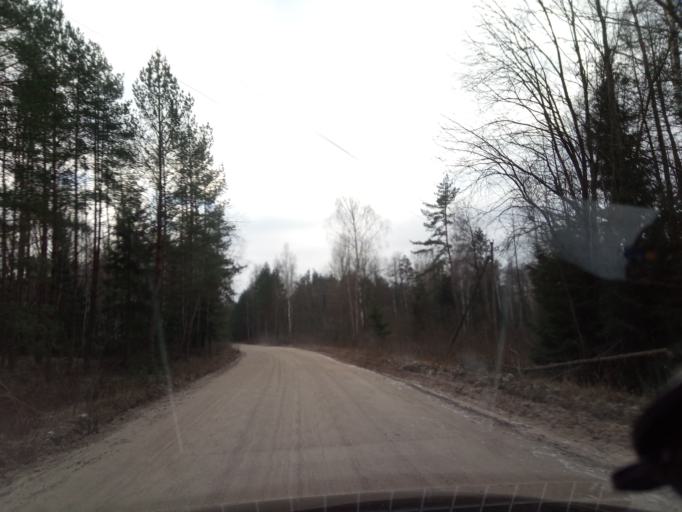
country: LT
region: Alytaus apskritis
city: Varena
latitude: 54.0222
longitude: 24.3467
